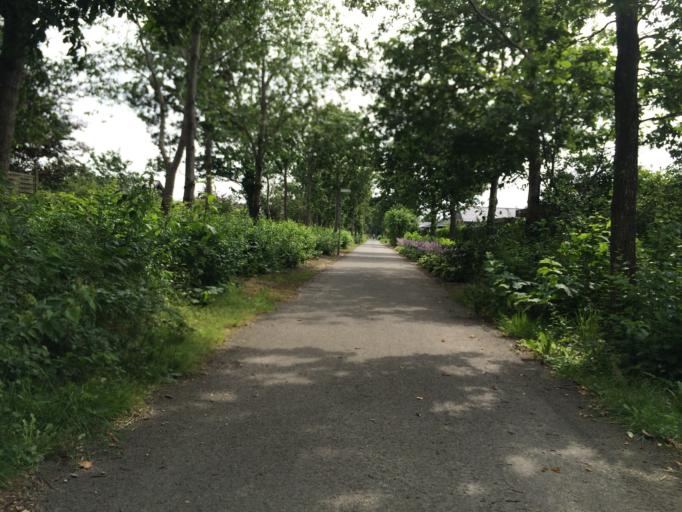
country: DK
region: Central Jutland
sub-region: Holstebro Kommune
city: Ulfborg
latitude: 56.2766
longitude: 8.3132
